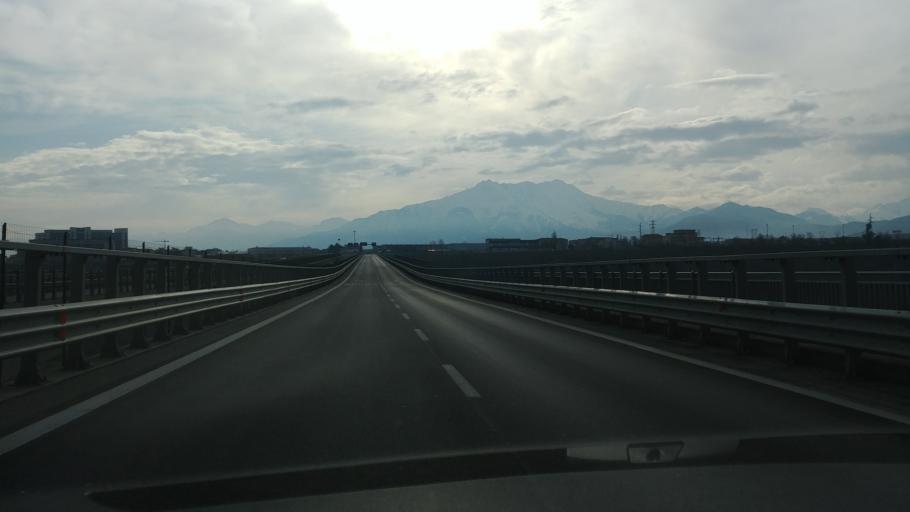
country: IT
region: Piedmont
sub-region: Provincia di Cuneo
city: Cuneo
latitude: 44.3862
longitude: 7.5220
